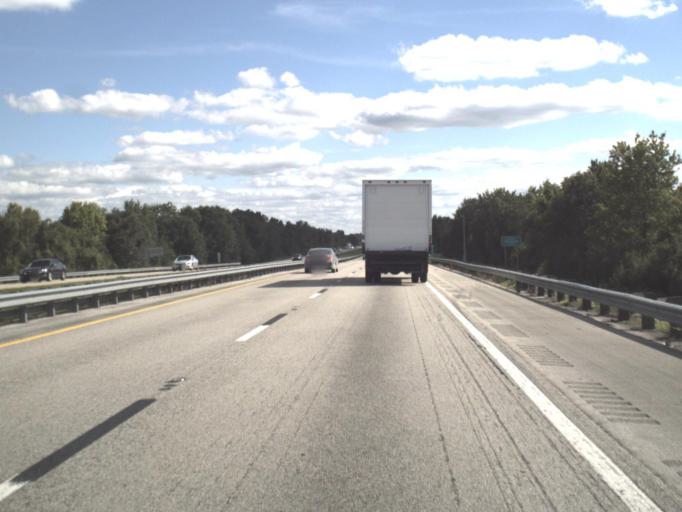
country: US
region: Florida
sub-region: Indian River County
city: Fellsmere
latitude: 27.6436
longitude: -80.8541
